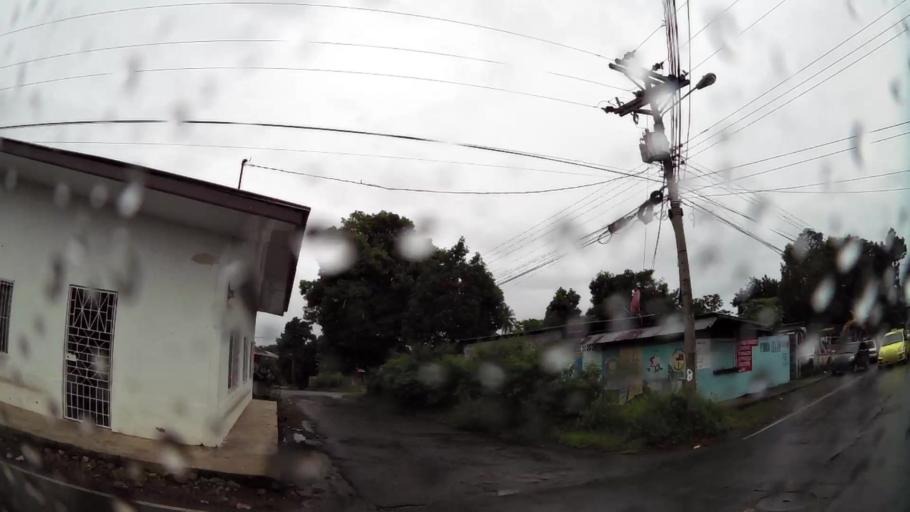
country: PA
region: Chiriqui
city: David
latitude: 8.4277
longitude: -82.4227
